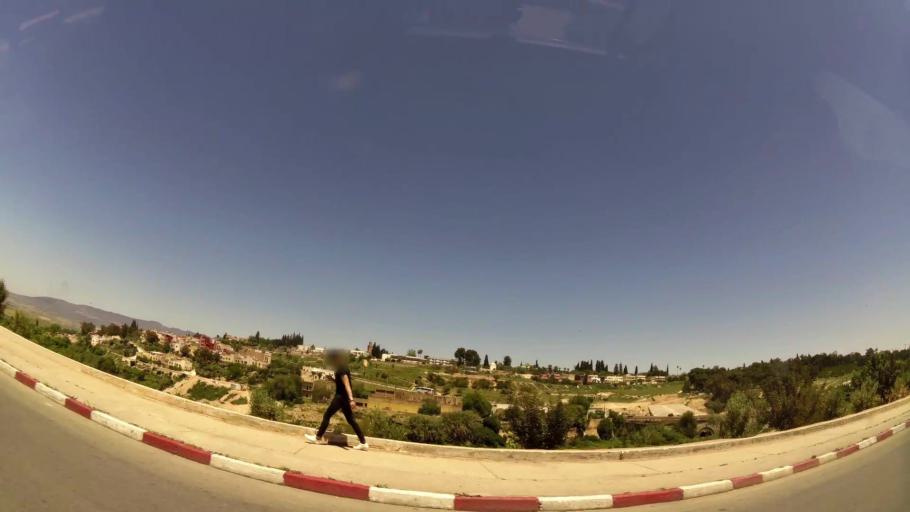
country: MA
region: Meknes-Tafilalet
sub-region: Meknes
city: Meknes
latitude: 33.9008
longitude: -5.5655
